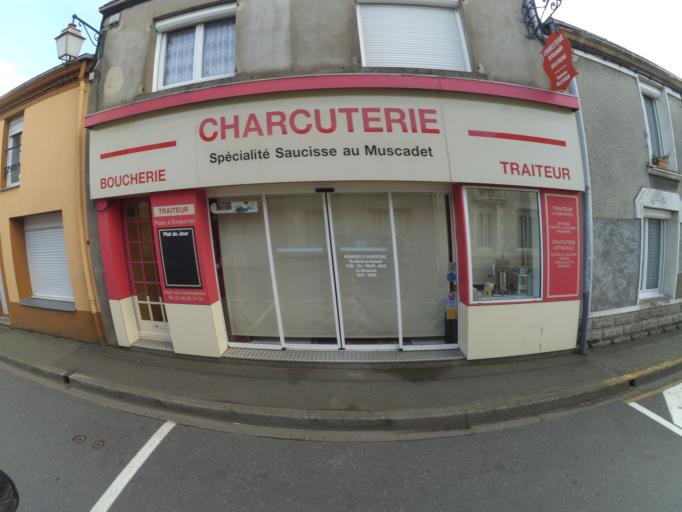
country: FR
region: Pays de la Loire
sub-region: Departement de la Loire-Atlantique
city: La Chapelle-Heulin
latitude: 47.1756
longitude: -1.3413
